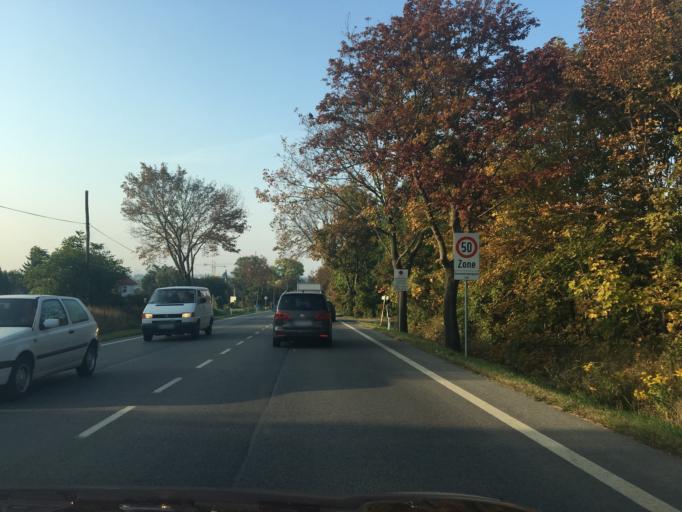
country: AT
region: Lower Austria
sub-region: Politischer Bezirk Korneuburg
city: Hagenbrunn
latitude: 48.3047
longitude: 16.4247
